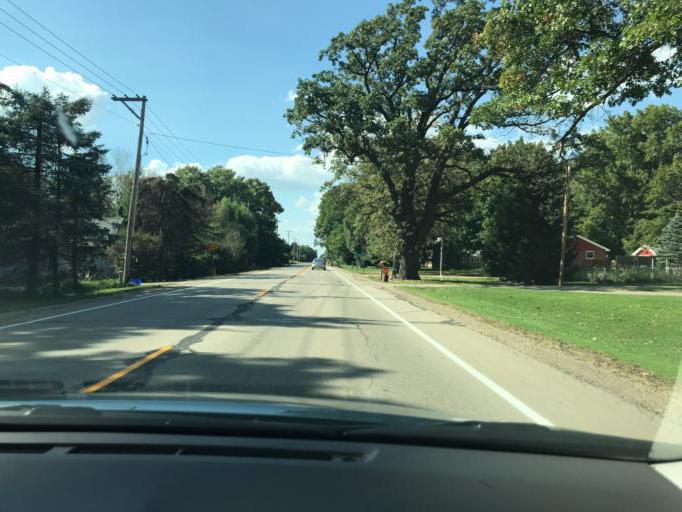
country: US
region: Wisconsin
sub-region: Walworth County
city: Williams Bay
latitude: 42.6077
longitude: -88.5574
